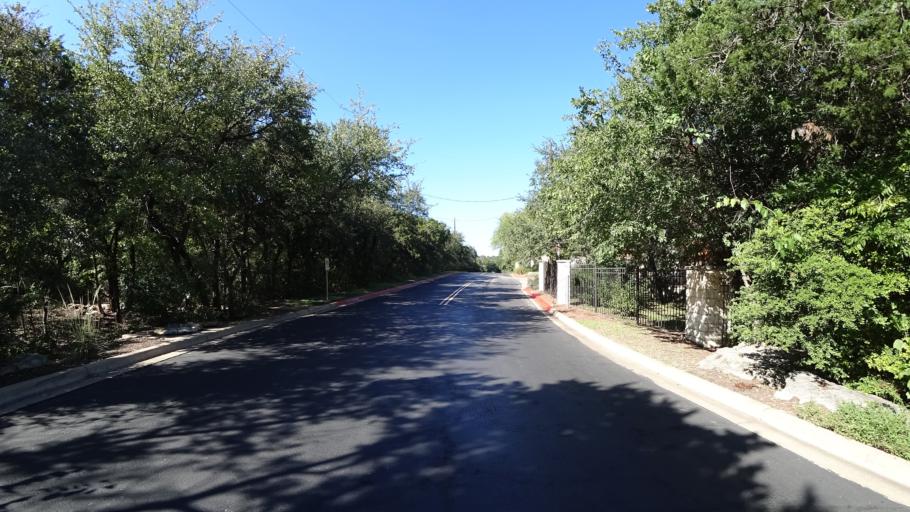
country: US
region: Texas
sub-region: Travis County
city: Rollingwood
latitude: 30.2545
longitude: -97.7974
